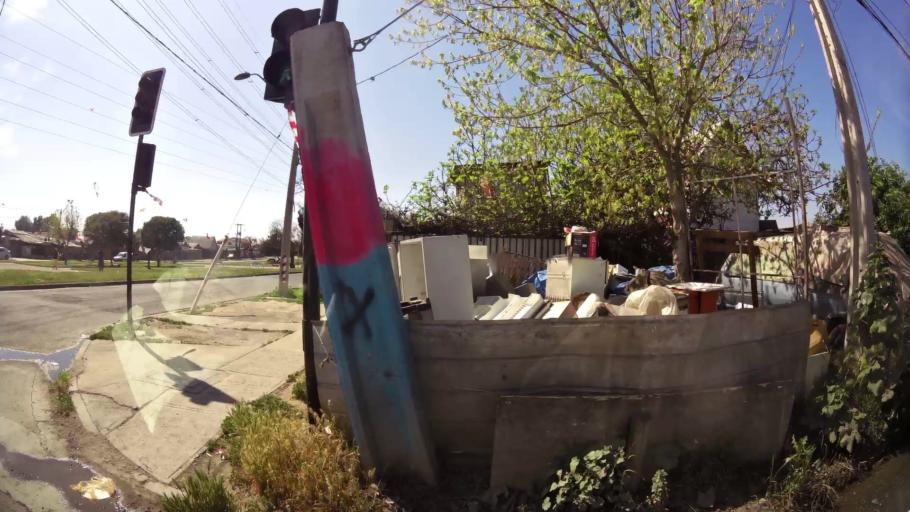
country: CL
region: Santiago Metropolitan
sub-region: Provincia de Santiago
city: Lo Prado
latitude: -33.5033
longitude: -70.7344
